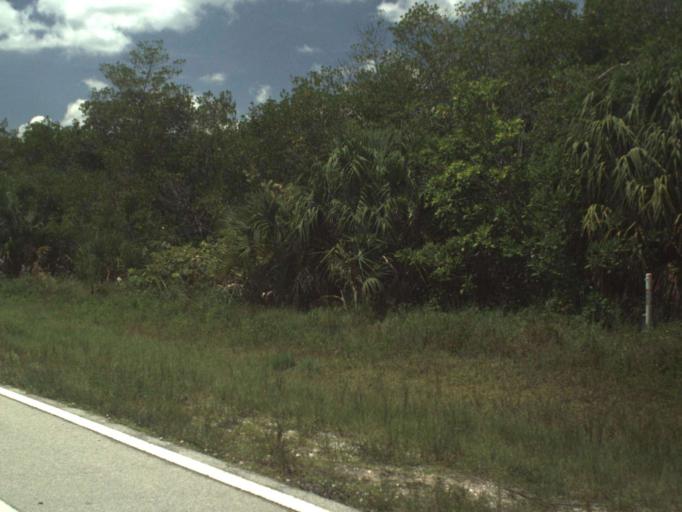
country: US
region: Florida
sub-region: Saint Lucie County
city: Hutchinson Island South
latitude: 27.3365
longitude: -80.2356
